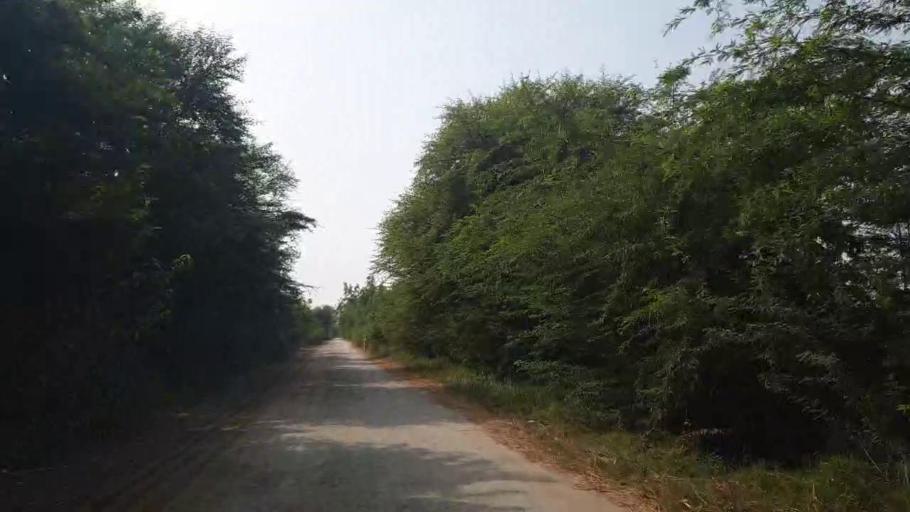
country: PK
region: Sindh
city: Badin
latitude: 24.7581
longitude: 68.7554
